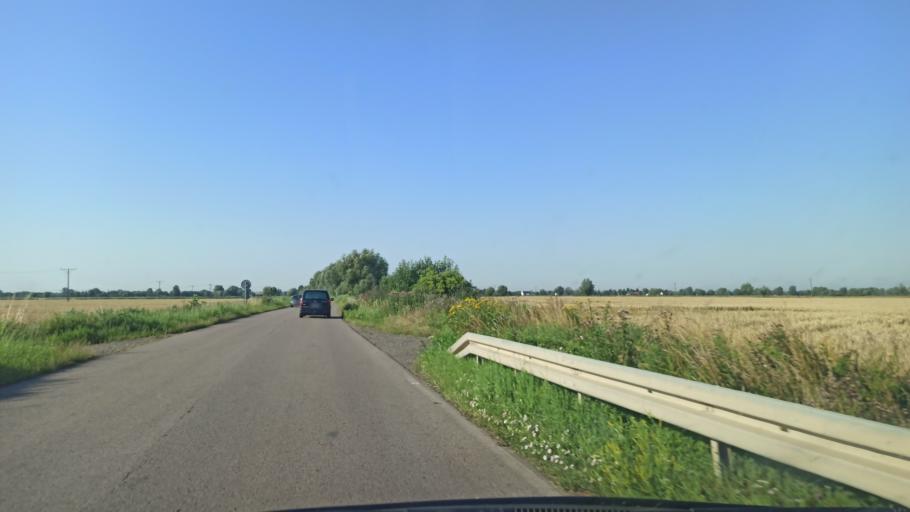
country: PL
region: Warmian-Masurian Voivodeship
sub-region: Powiat elblaski
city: Elblag
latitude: 54.1852
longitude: 19.3329
